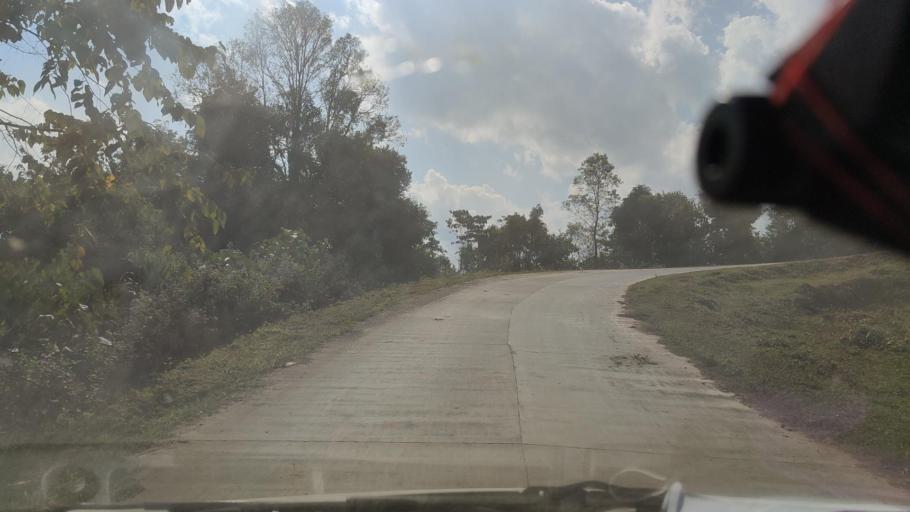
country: CN
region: Yunnan
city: Nayun
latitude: 21.8139
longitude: 98.8448
